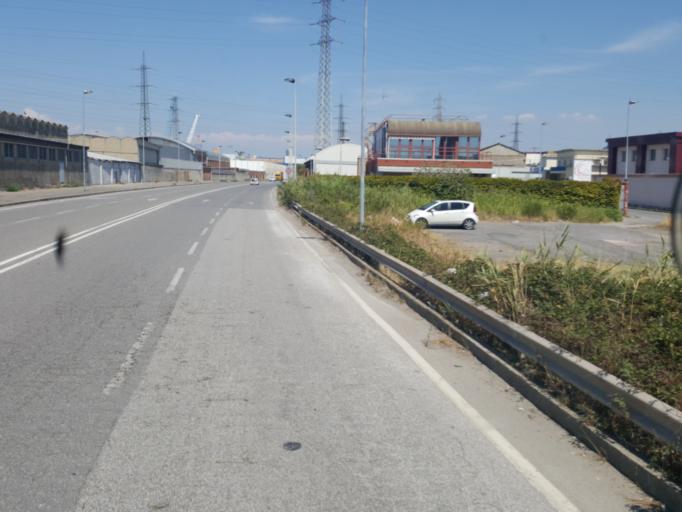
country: IT
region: Tuscany
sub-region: Provincia di Livorno
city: Livorno
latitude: 43.5674
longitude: 10.3135
